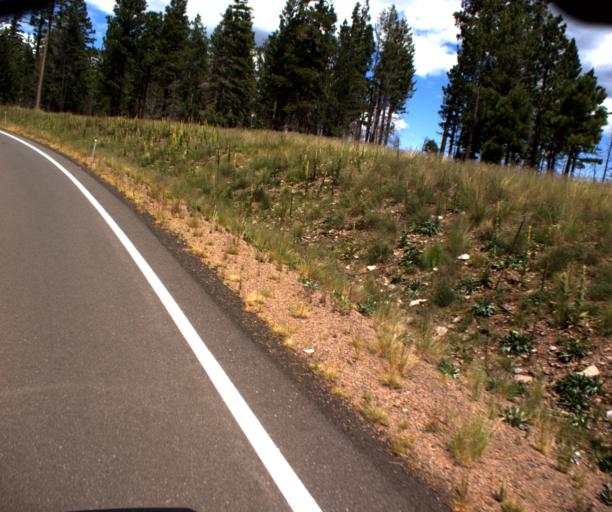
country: US
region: Arizona
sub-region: Apache County
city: Eagar
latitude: 33.9247
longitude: -109.4541
